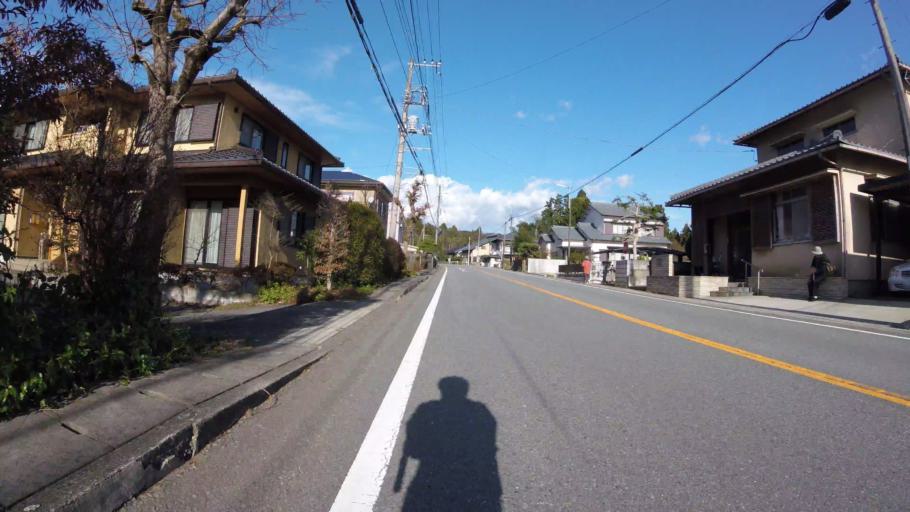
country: JP
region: Kanagawa
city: Hakone
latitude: 35.1558
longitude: 138.9954
